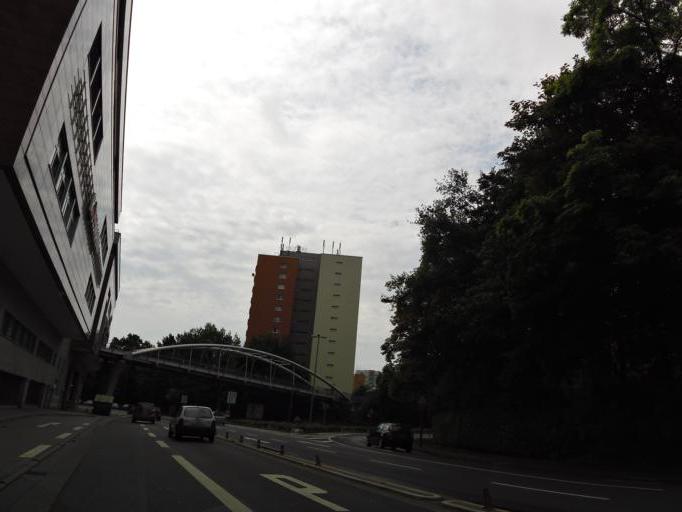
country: DE
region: Hesse
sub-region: Regierungsbezirk Darmstadt
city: Steinbach am Taunus
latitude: 50.1578
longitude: 8.6330
